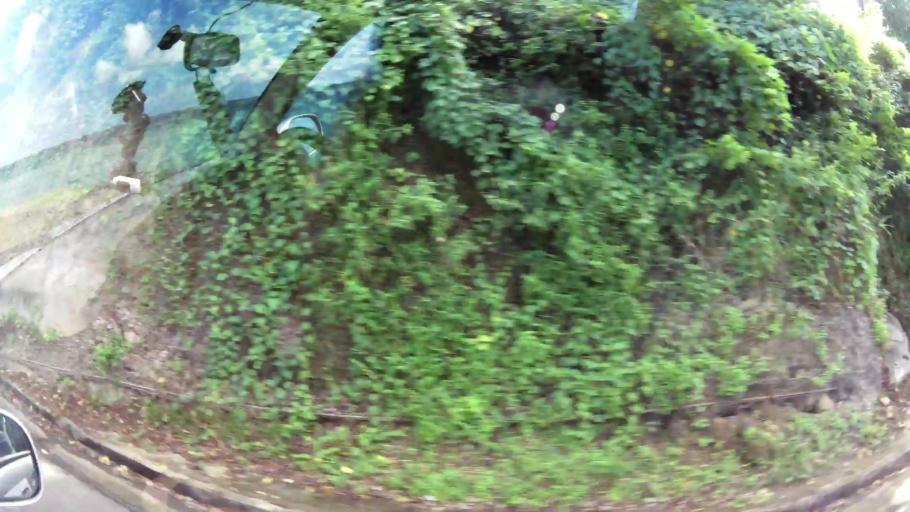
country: GD
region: Saint Mark
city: Victoria
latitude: 12.1985
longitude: -61.7033
